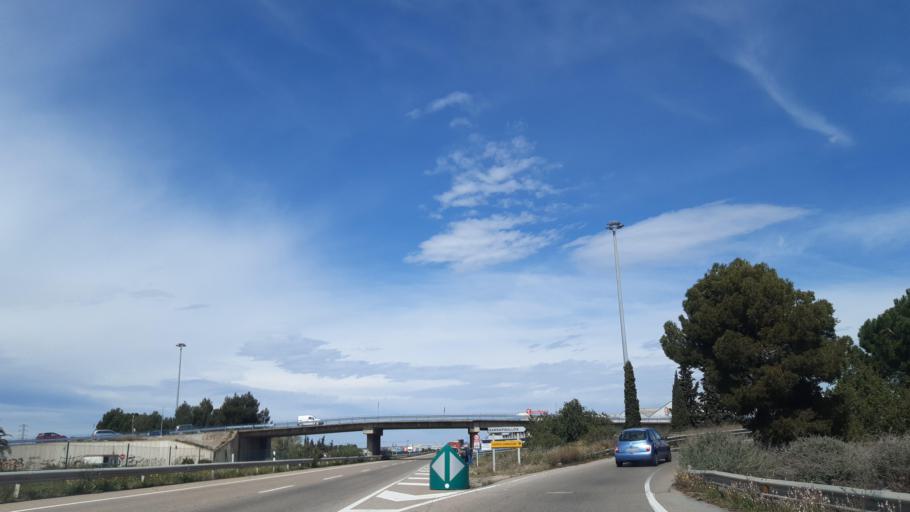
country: ES
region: Aragon
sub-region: Provincia de Zaragoza
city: Utebo
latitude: 41.7038
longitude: -1.0035
